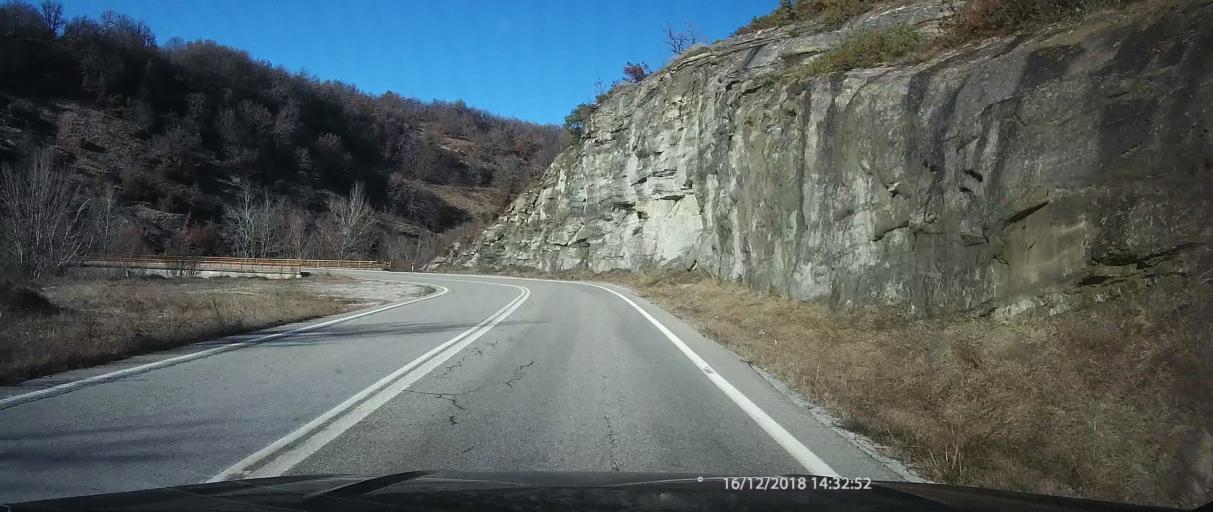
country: GR
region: West Macedonia
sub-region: Nomos Kozanis
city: Tsotili
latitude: 40.1970
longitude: 21.1664
